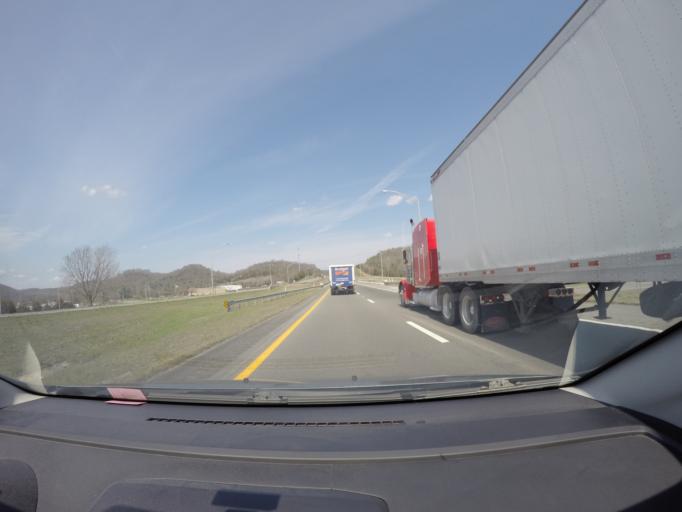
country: US
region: Tennessee
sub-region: Davidson County
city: Goodlettsville
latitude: 36.2761
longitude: -86.7987
